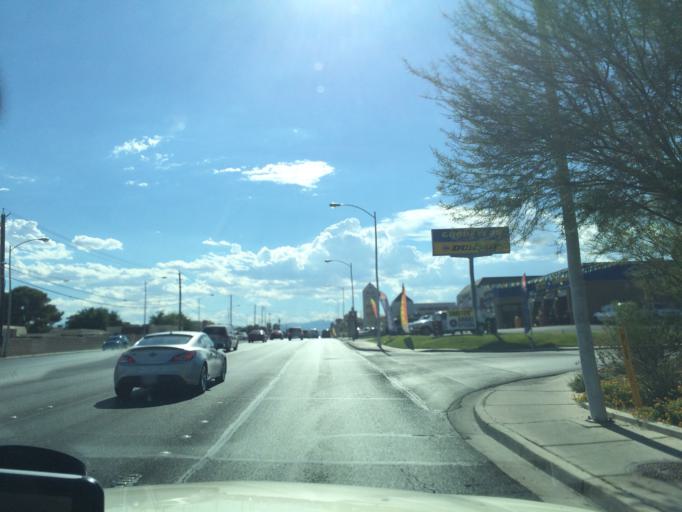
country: US
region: Nevada
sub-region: Clark County
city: Whitney
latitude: 36.1002
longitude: -115.0963
